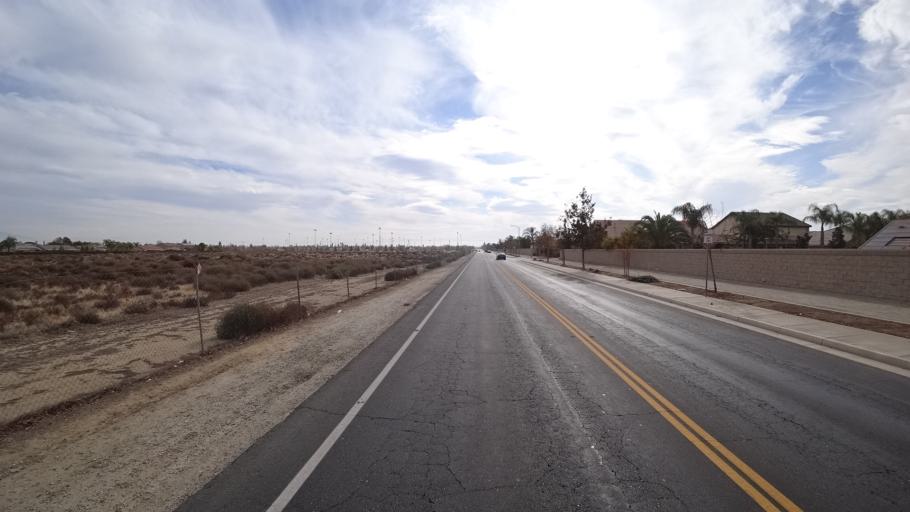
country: US
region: California
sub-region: Kern County
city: Rosedale
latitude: 35.4083
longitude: -119.1367
